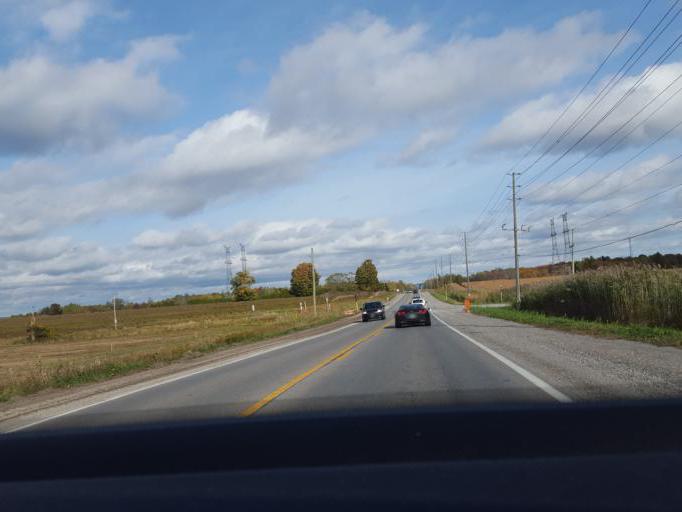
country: CA
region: Ontario
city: Oshawa
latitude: 43.9584
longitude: -78.7680
